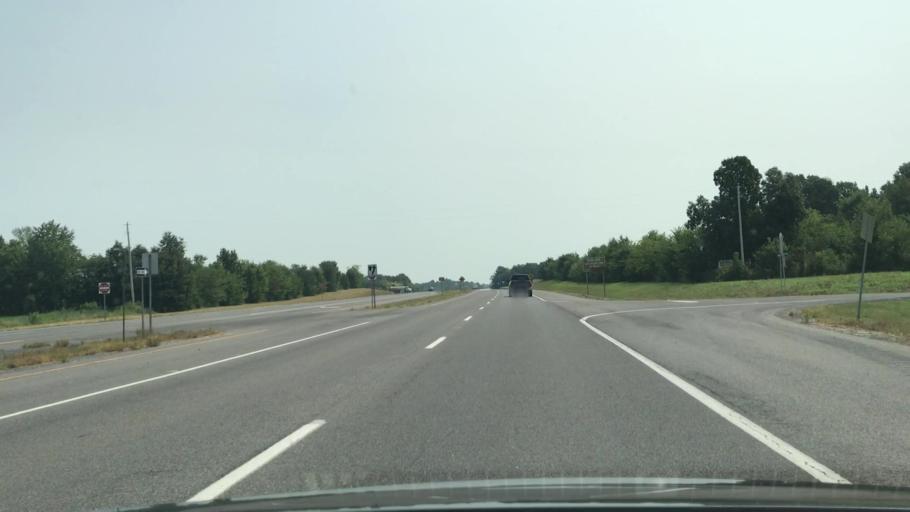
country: US
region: Kentucky
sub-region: Calloway County
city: Murray
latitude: 36.6495
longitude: -88.2380
